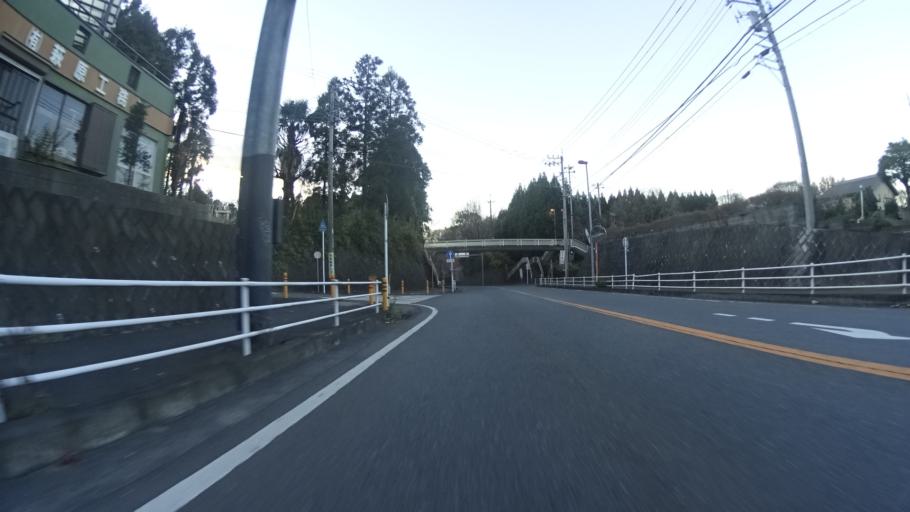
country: JP
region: Kanagawa
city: Zama
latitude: 35.5295
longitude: 139.3655
